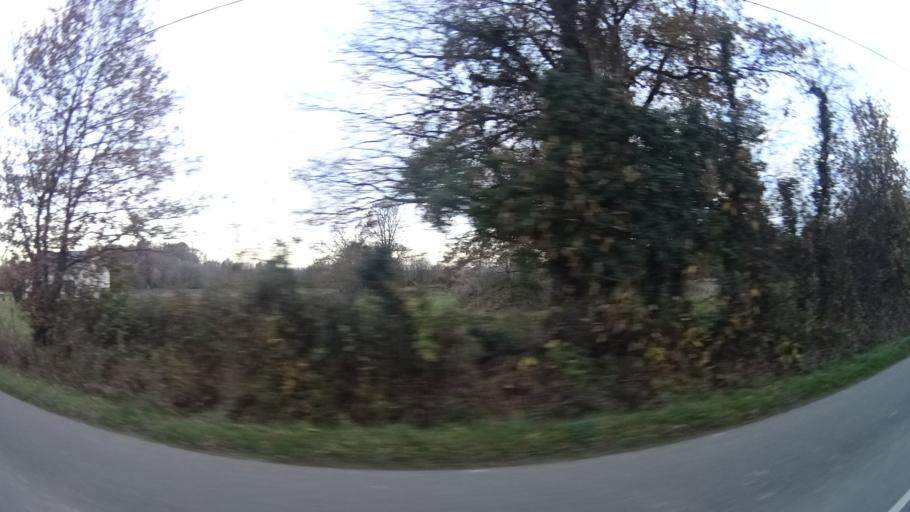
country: FR
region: Brittany
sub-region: Departement d'Ille-et-Vilaine
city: Langon
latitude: 47.6746
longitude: -1.8992
